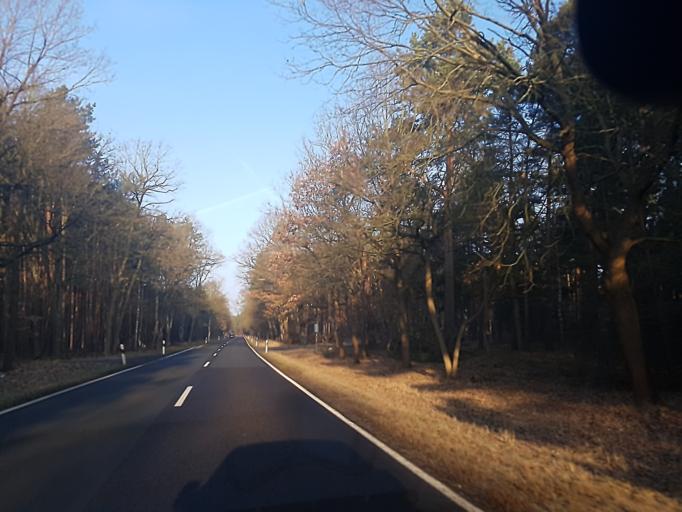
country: DE
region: Brandenburg
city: Bruck
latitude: 52.2217
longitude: 12.7289
